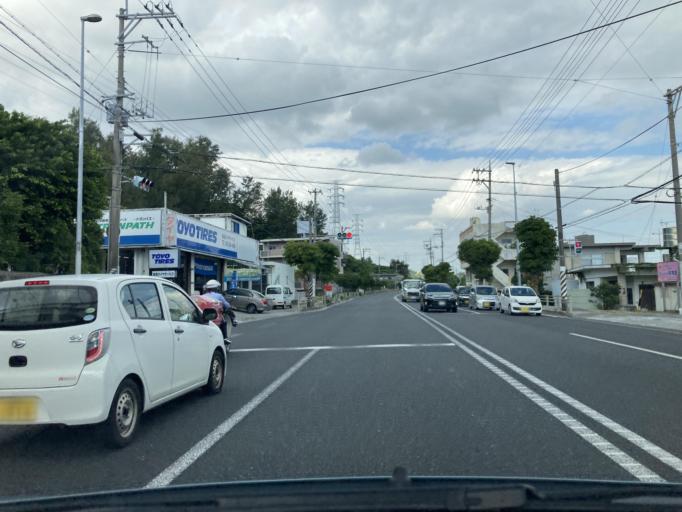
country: JP
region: Okinawa
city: Ginowan
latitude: 26.2485
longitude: 127.7822
